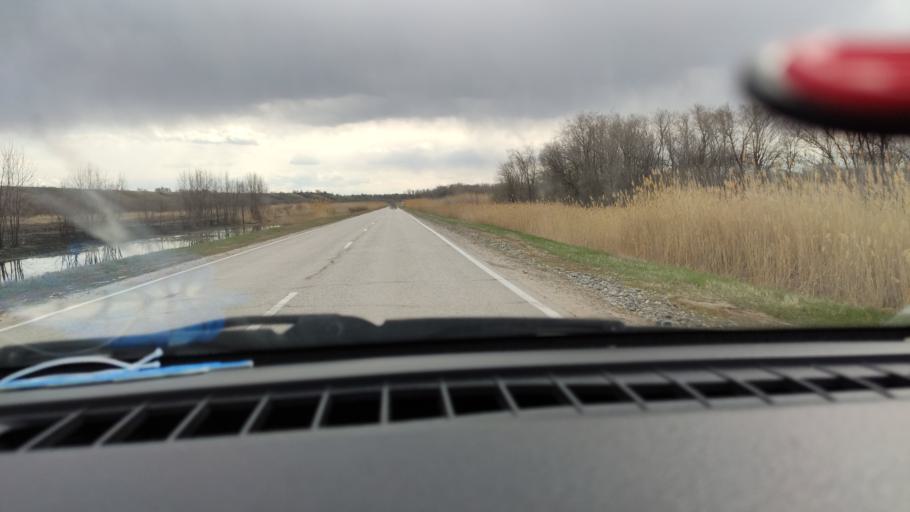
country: RU
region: Saratov
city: Privolzhskiy
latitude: 51.2606
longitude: 45.9453
